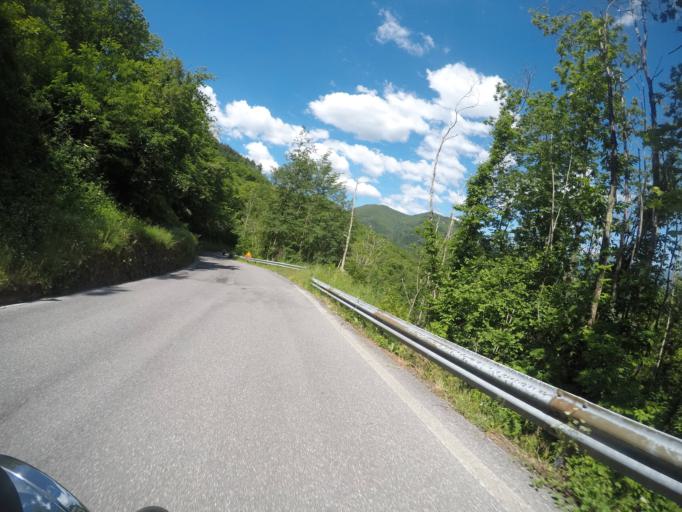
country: IT
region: Tuscany
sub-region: Provincia di Lucca
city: Careggine
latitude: 44.1351
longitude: 10.3453
